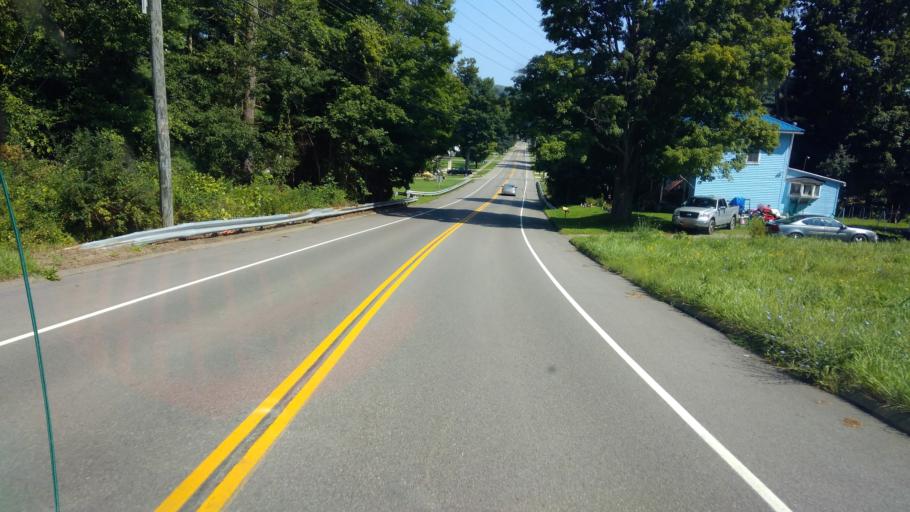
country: US
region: New York
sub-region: Allegany County
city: Belmont
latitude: 42.3014
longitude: -78.0257
